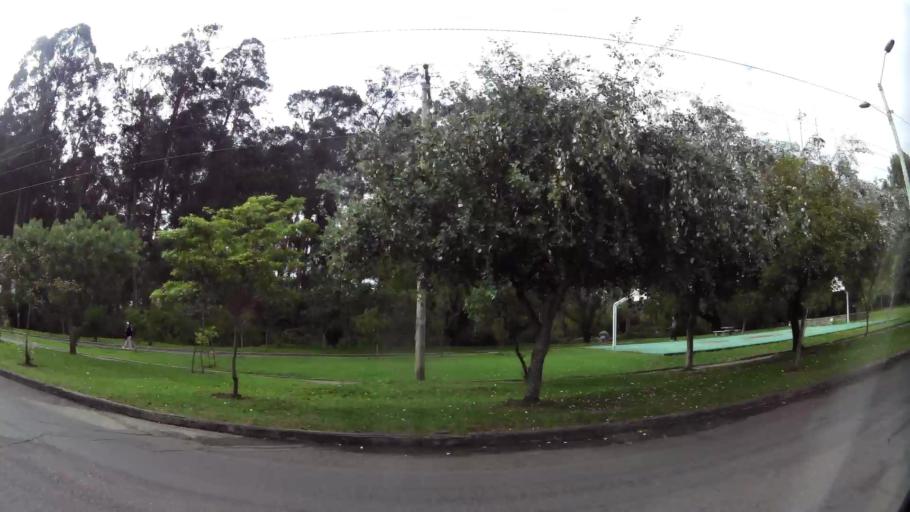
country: EC
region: Azuay
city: Cuenca
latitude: -2.9078
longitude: -78.9873
